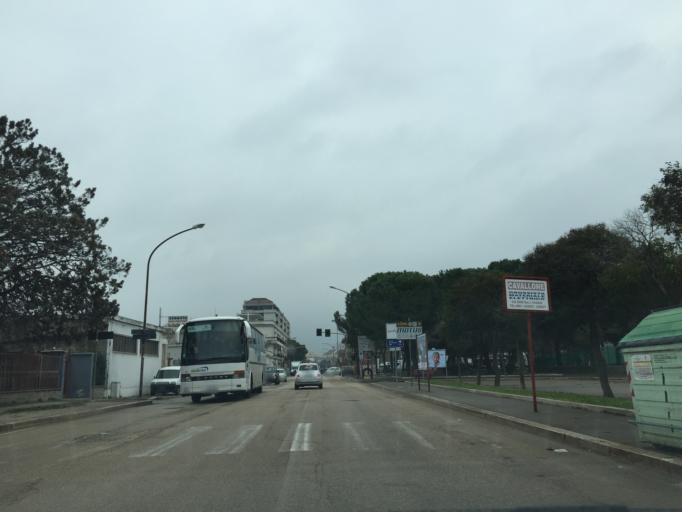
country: IT
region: Apulia
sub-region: Provincia di Foggia
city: Foggia
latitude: 41.4712
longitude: 15.5382
